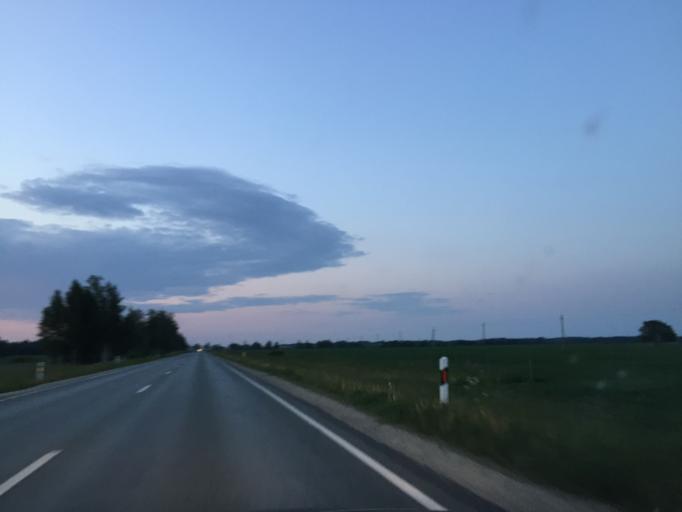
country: LT
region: Siauliu apskritis
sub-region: Joniskis
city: Joniskis
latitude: 56.1138
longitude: 23.4924
